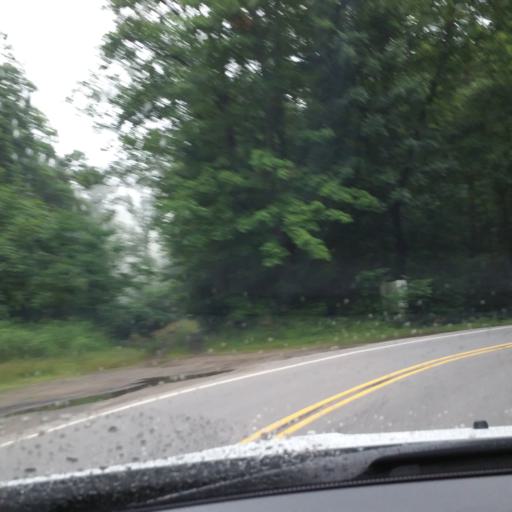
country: US
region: North Carolina
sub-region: Mitchell County
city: Spruce Pine
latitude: 35.7740
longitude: -82.1757
